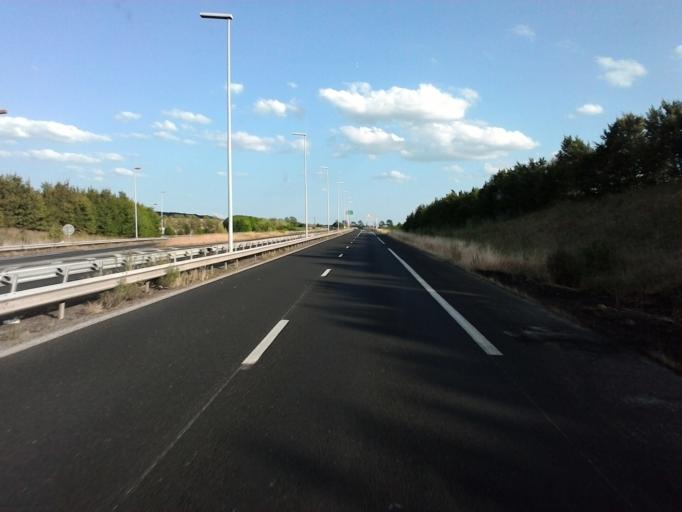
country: FR
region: Lorraine
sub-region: Departement de Meurthe-et-Moselle
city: Flavigny-sur-Moselle
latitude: 48.5563
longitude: 6.1869
